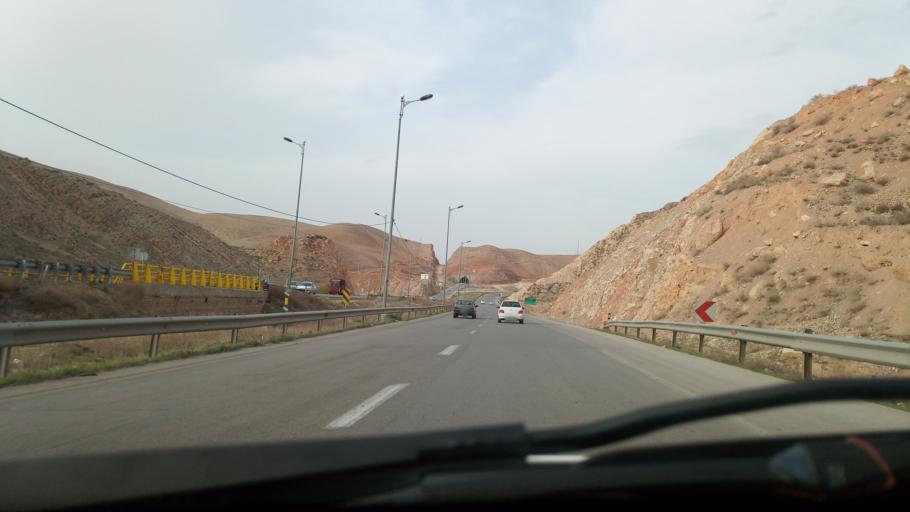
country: IR
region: Khorasan-e Shomali
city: Bojnurd
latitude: 37.4912
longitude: 57.4409
